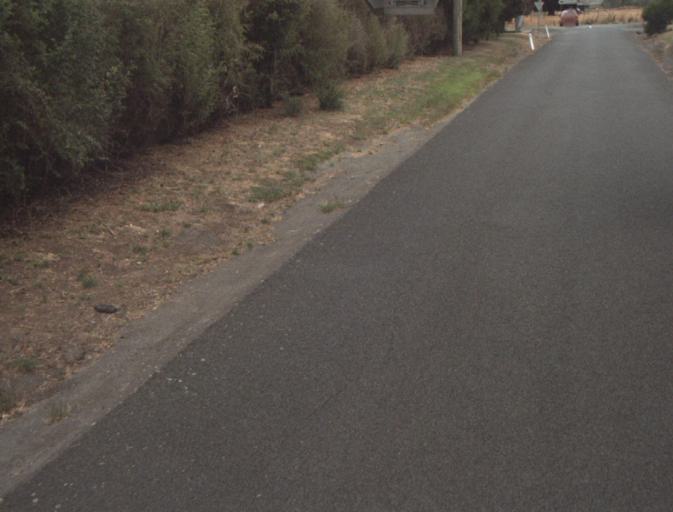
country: AU
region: Tasmania
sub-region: Northern Midlands
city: Evandale
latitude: -41.5055
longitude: 147.2550
